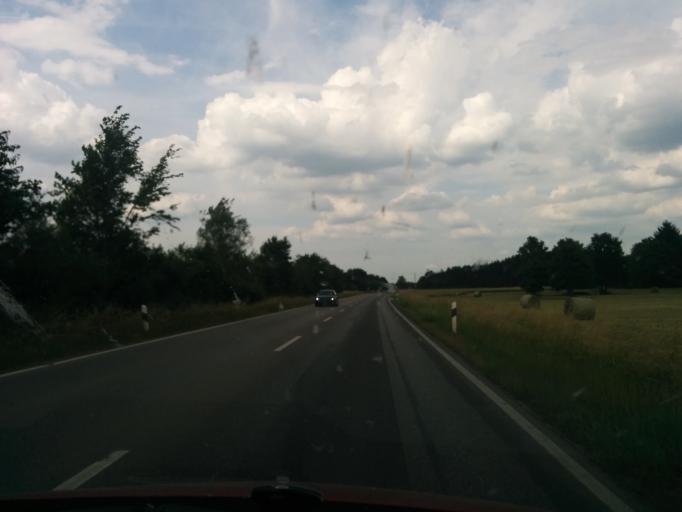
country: DE
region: Bavaria
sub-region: Swabia
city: Bad Worishofen
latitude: 48.0221
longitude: 10.6101
